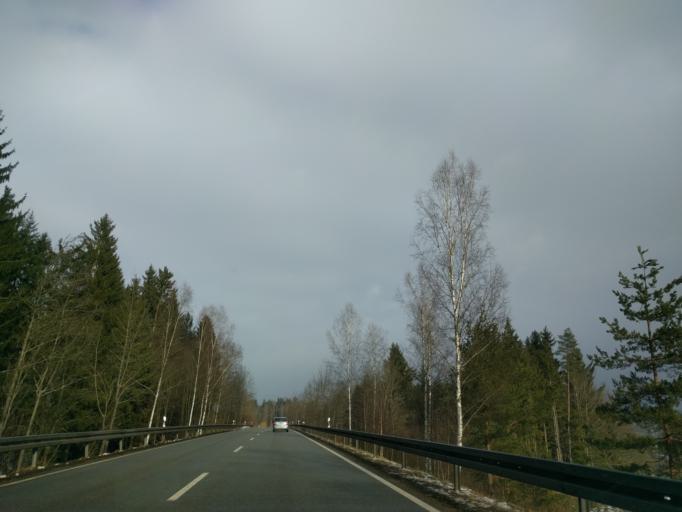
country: DE
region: Bavaria
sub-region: Lower Bavaria
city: Zwiesel
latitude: 49.0219
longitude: 13.2482
